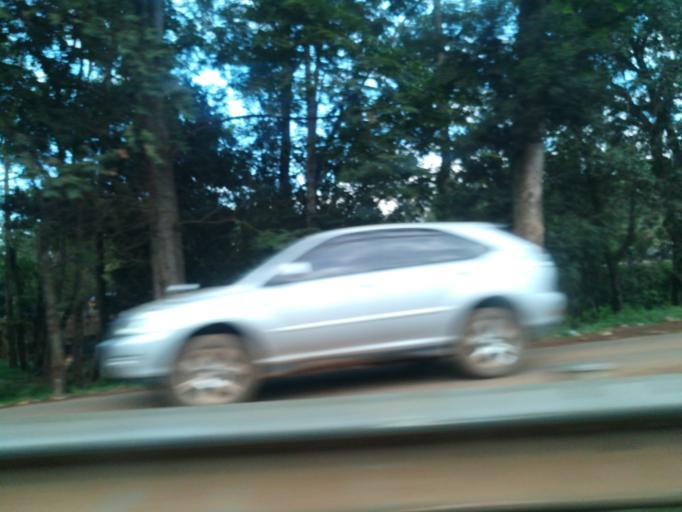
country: KE
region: Nairobi Area
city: Thika
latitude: -1.0268
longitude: 37.0657
